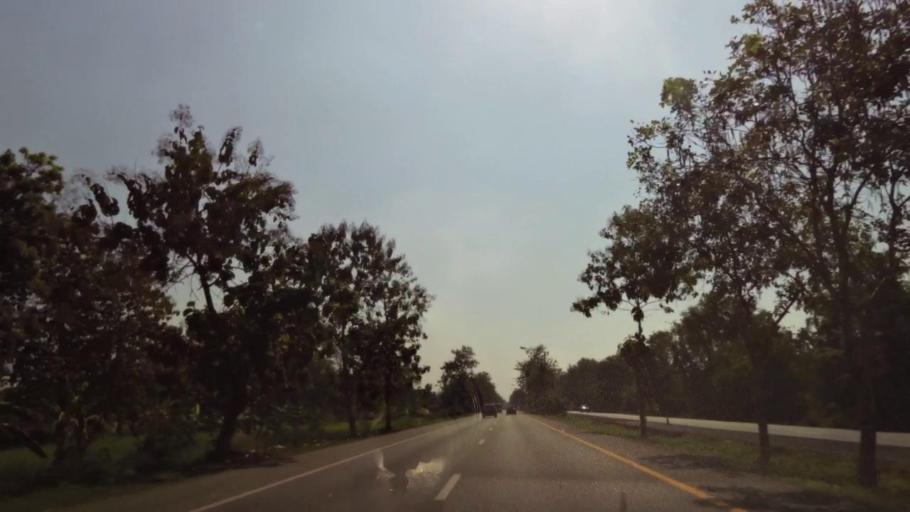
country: TH
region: Phichit
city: Bueng Na Rang
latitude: 16.0761
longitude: 100.1242
